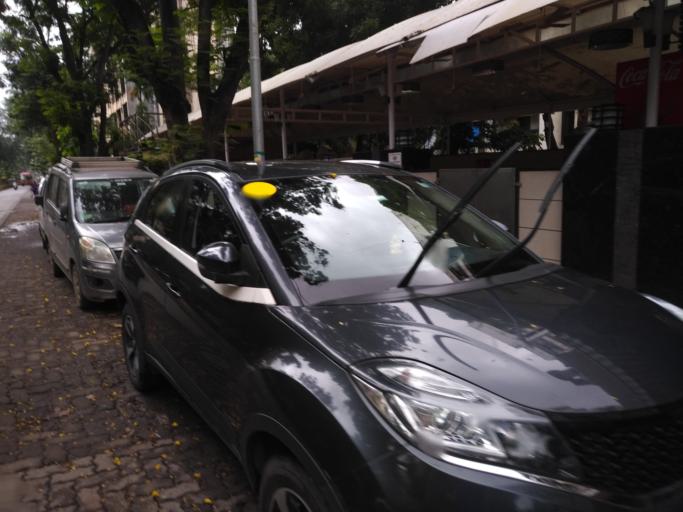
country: IN
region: Maharashtra
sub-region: Mumbai Suburban
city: Borivli
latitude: 19.2433
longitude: 72.8652
